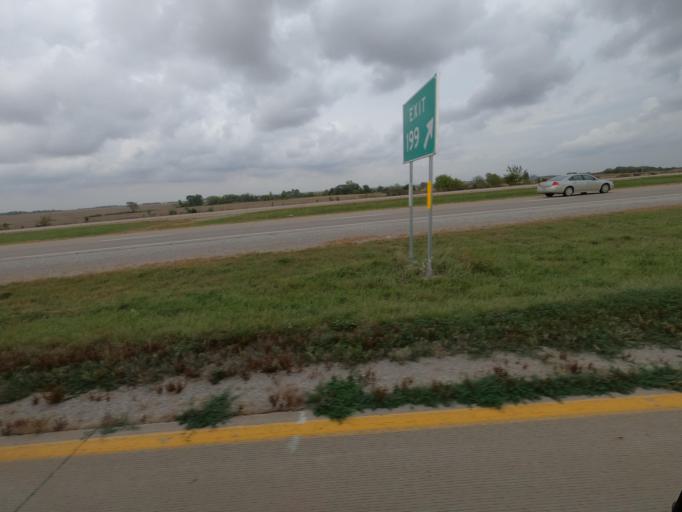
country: US
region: Iowa
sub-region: Wapello County
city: Ottumwa
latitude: 40.9997
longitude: -92.2423
